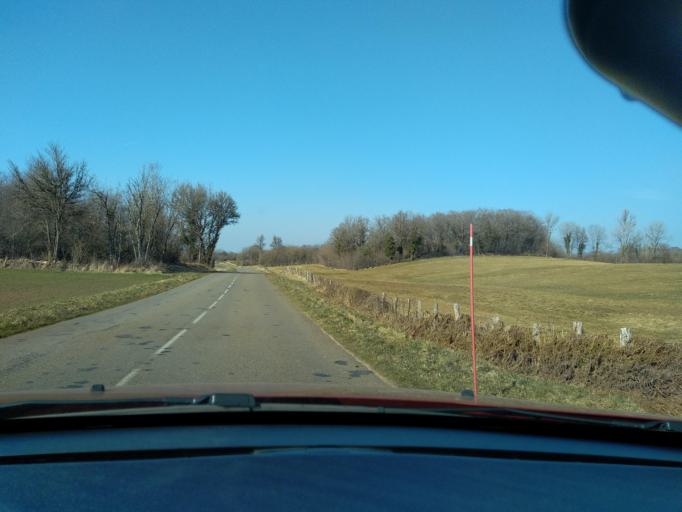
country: FR
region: Franche-Comte
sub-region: Departement du Jura
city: Perrigny
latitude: 46.6177
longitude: 5.6415
